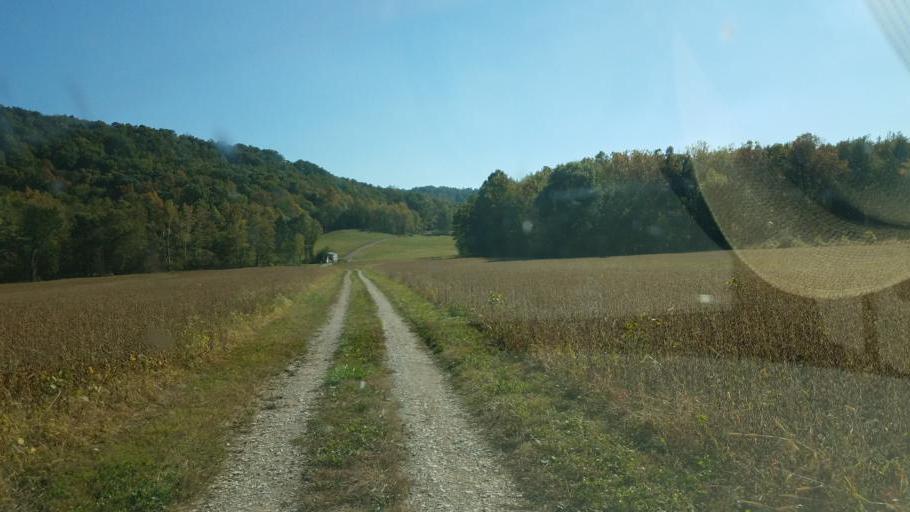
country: US
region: Kentucky
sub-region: Fleming County
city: Flemingsburg
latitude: 38.4655
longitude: -83.5611
